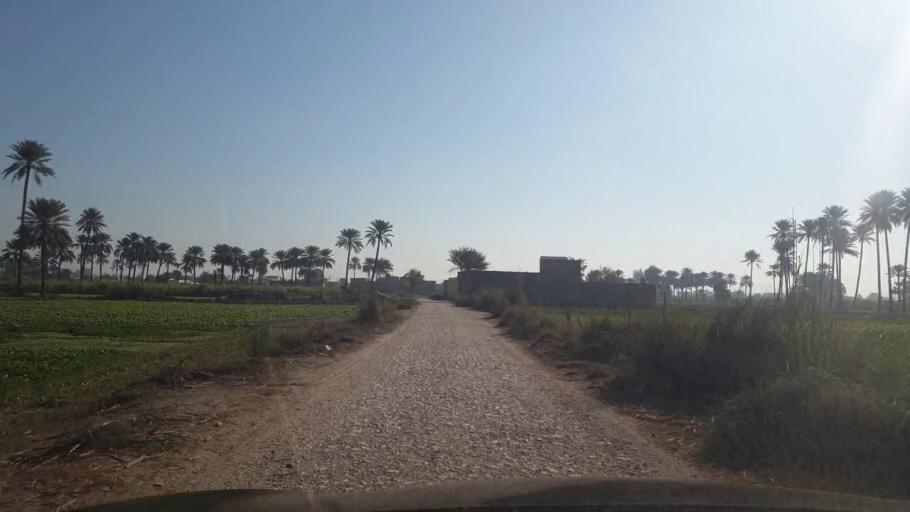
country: PK
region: Sindh
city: Ghotki
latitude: 27.9940
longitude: 69.3215
